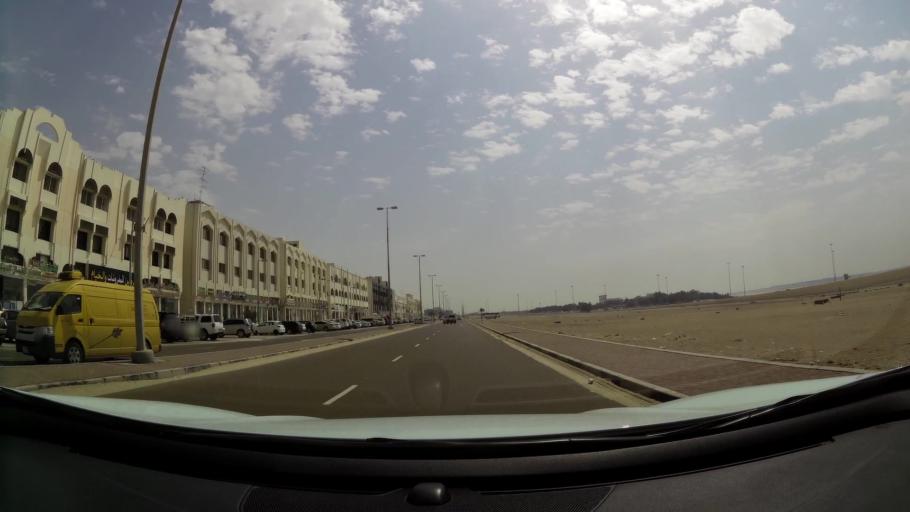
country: AE
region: Abu Dhabi
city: Abu Dhabi
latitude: 24.3101
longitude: 54.6061
